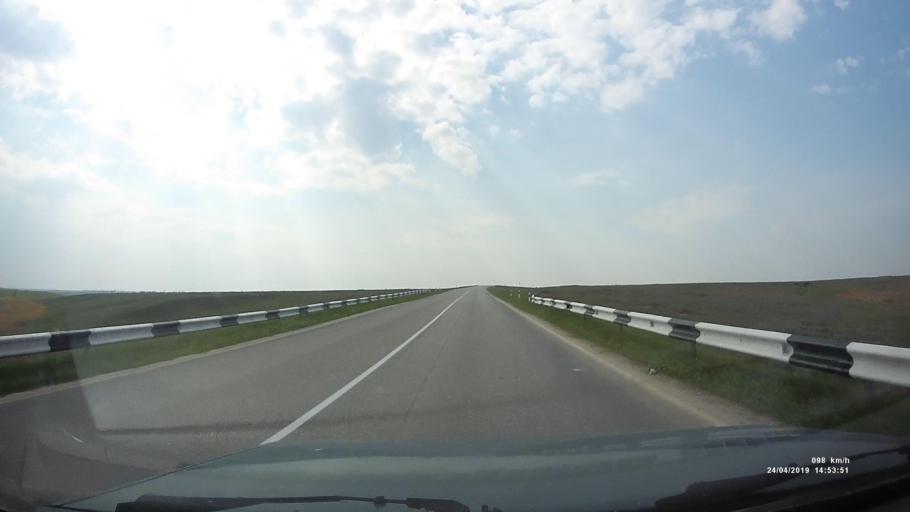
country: RU
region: Rostov
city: Remontnoye
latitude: 46.5318
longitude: 43.6502
